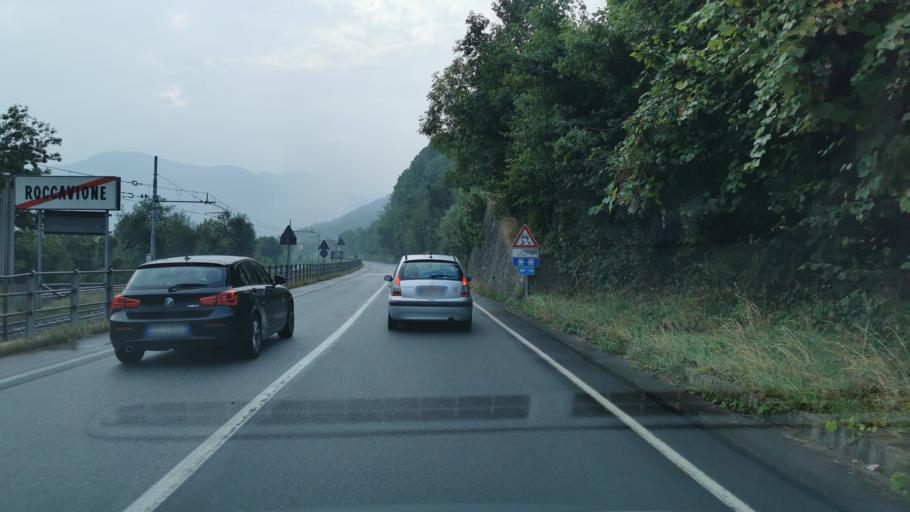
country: IT
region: Piedmont
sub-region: Provincia di Cuneo
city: Roccavione
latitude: 44.3121
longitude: 7.4872
